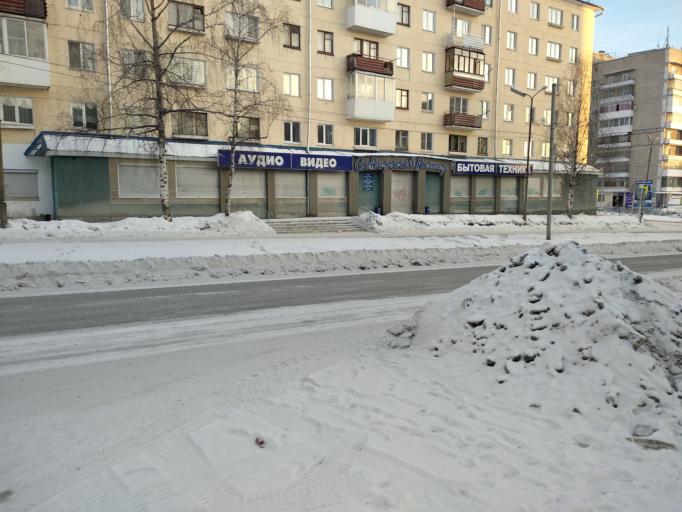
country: RU
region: Sverdlovsk
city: Krasnotur'insk
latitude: 59.7626
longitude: 60.2079
